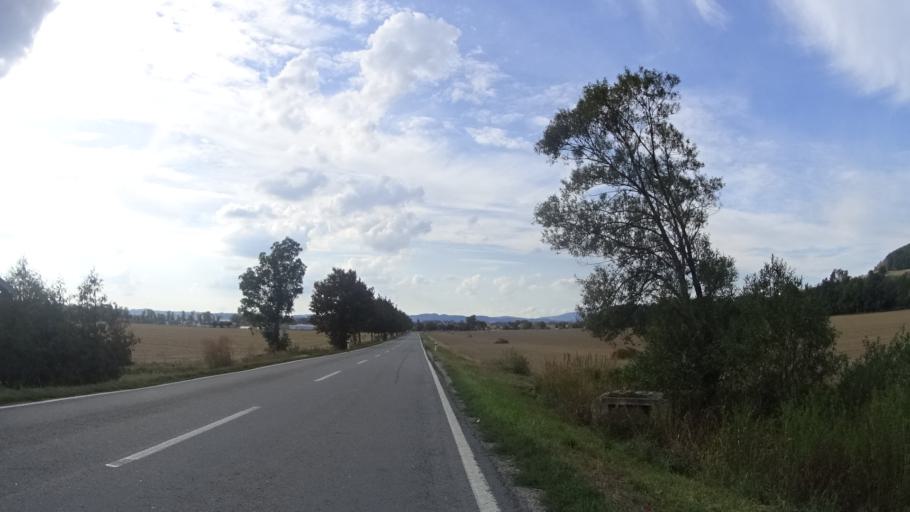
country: CZ
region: Olomoucky
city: Lestina
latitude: 49.8626
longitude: 16.9403
